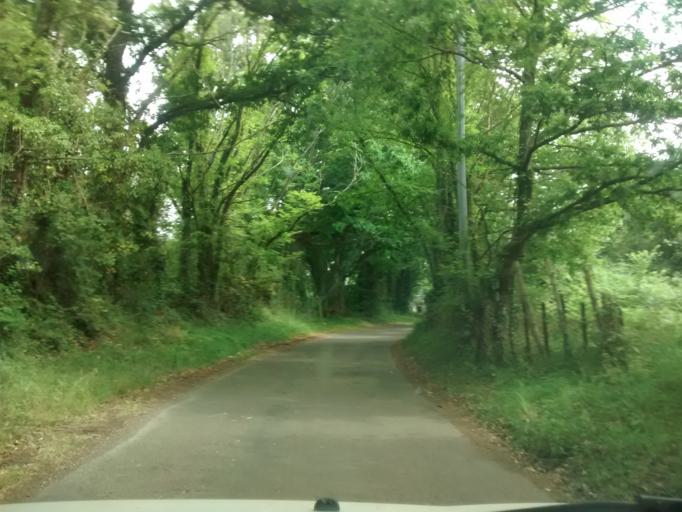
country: FR
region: Brittany
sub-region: Departement d'Ille-et-Vilaine
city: Saint-Jacques-de-la-Lande
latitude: 48.0874
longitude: -1.7292
